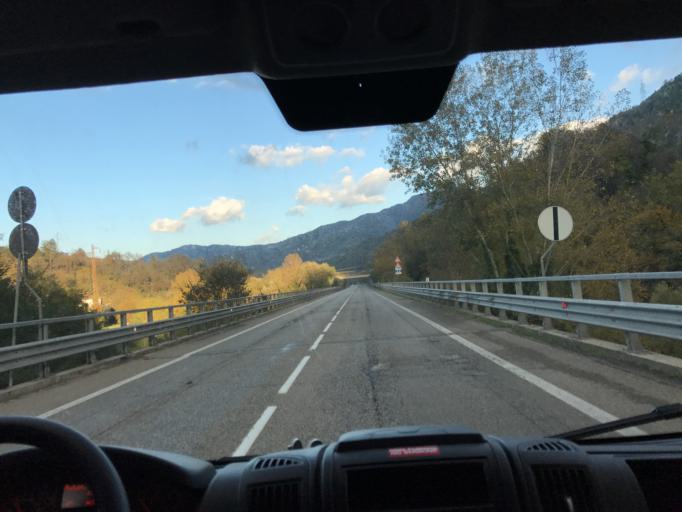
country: IT
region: The Marches
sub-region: Provincia di Ascoli Piceno
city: Marsia
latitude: 42.8021
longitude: 13.4755
